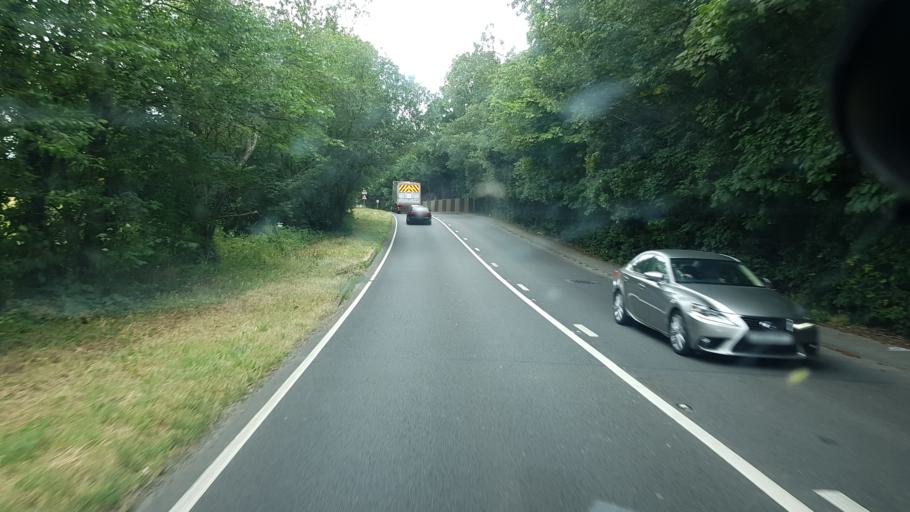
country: GB
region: England
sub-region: Surrey
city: Godstone
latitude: 51.2068
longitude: -0.0564
